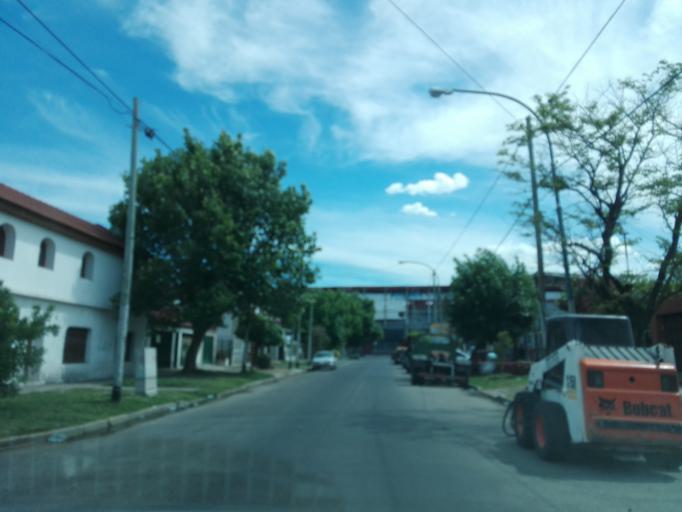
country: AR
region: Buenos Aires
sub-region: Partido de Lanus
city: Lanus
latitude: -34.7161
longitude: -58.3824
